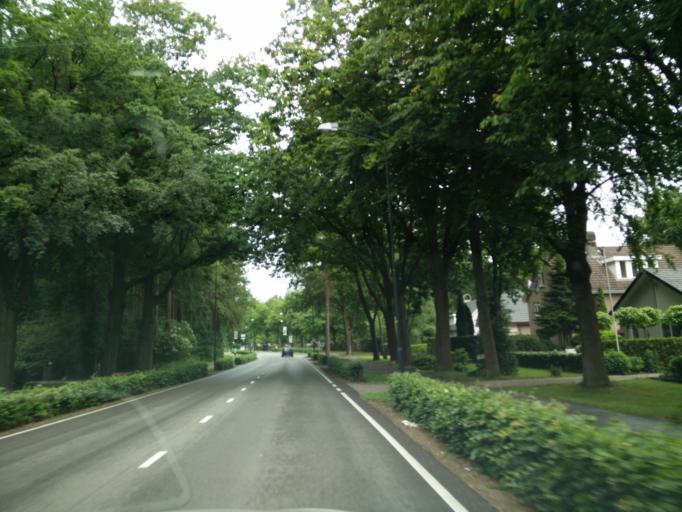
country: NL
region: Gelderland
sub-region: Gemeente Apeldoorn
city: Apeldoorn
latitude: 52.2127
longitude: 5.9287
